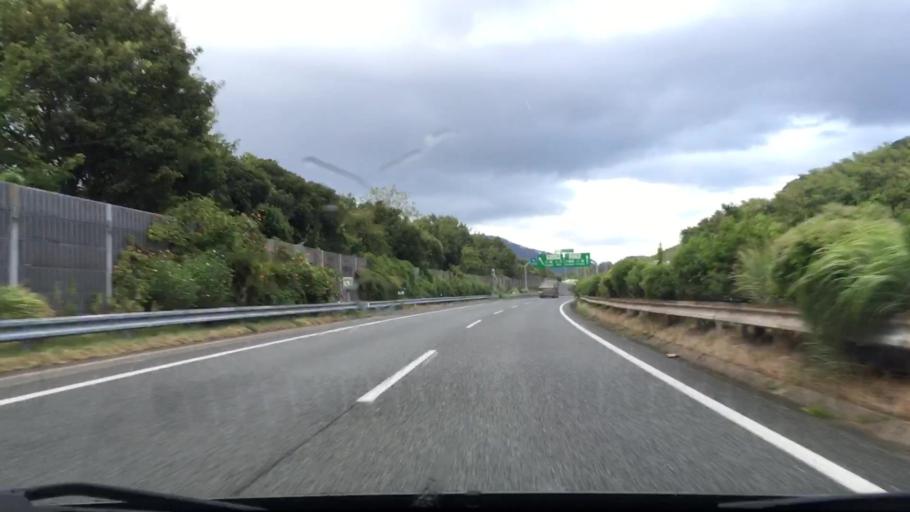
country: JP
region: Fukuoka
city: Kitakyushu
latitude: 33.8105
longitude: 130.8796
